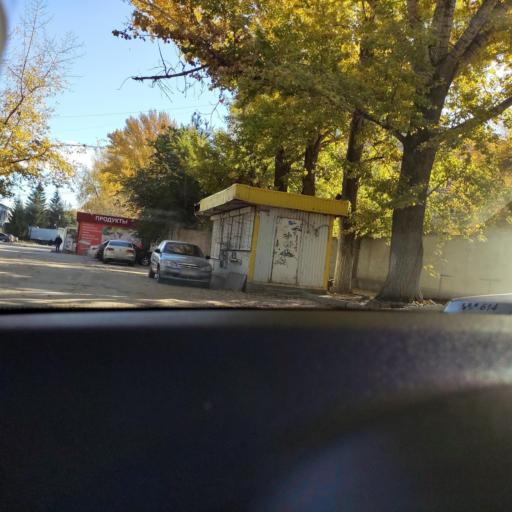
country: RU
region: Samara
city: Petra-Dubrava
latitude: 53.2318
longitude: 50.2930
